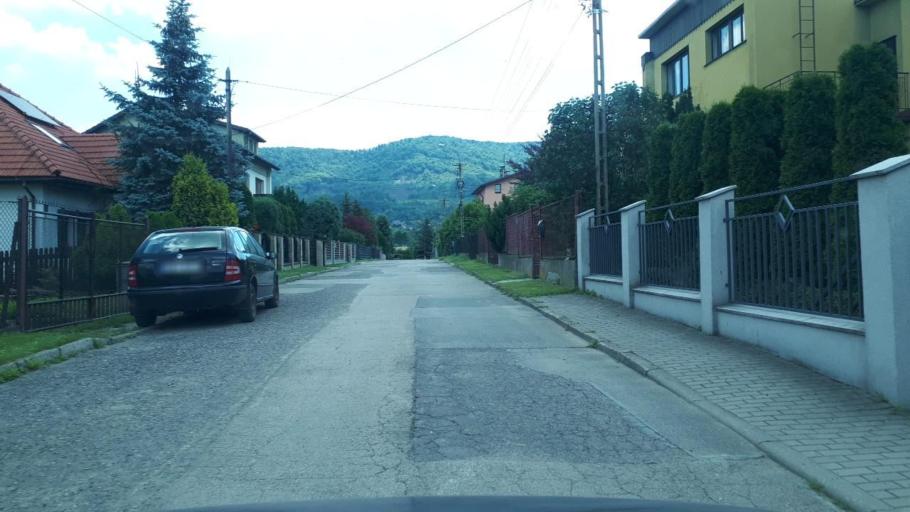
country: PL
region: Silesian Voivodeship
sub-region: Powiat bielski
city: Kozy
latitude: 49.8452
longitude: 19.1489
